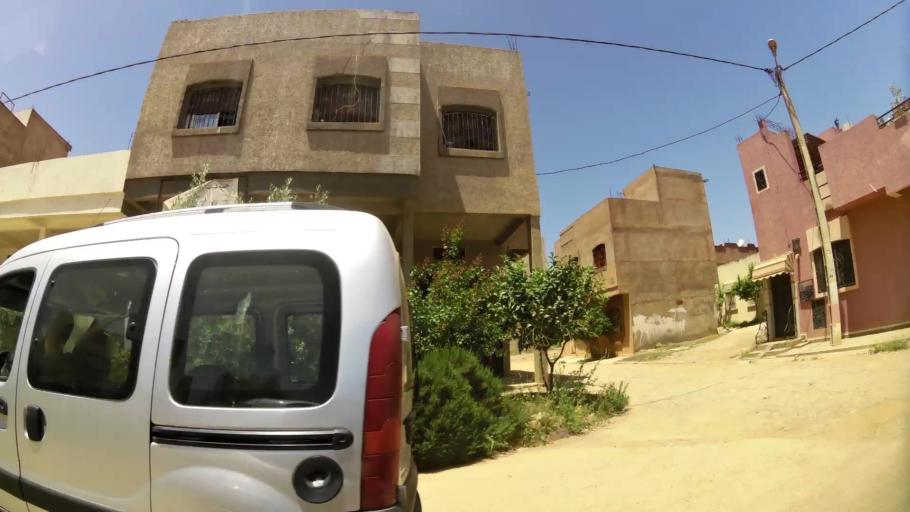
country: MA
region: Rabat-Sale-Zemmour-Zaer
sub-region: Khemisset
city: Khemisset
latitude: 33.8328
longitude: -6.0847
